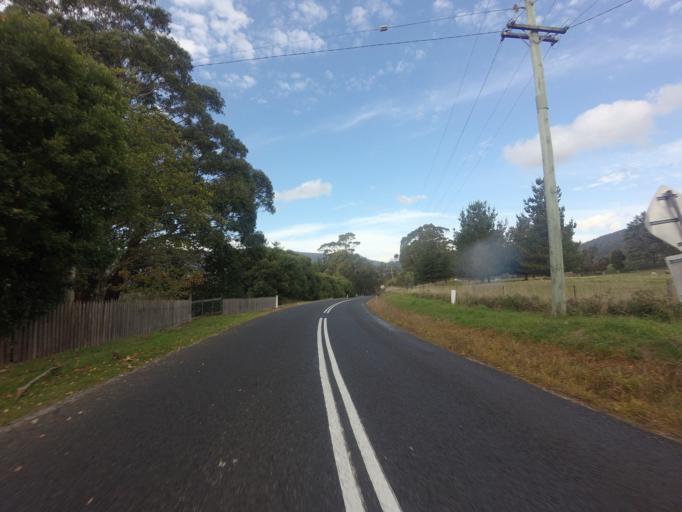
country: AU
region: Tasmania
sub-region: Meander Valley
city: Deloraine
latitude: -41.6215
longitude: 146.7024
